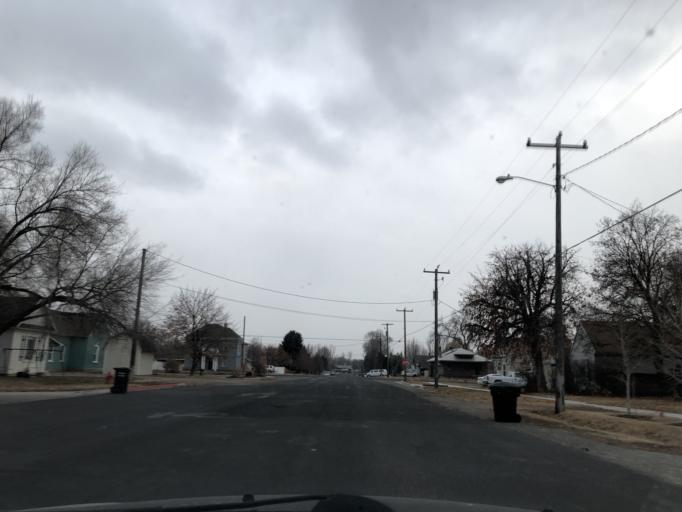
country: US
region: Utah
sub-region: Cache County
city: Logan
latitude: 41.7287
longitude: -111.8480
